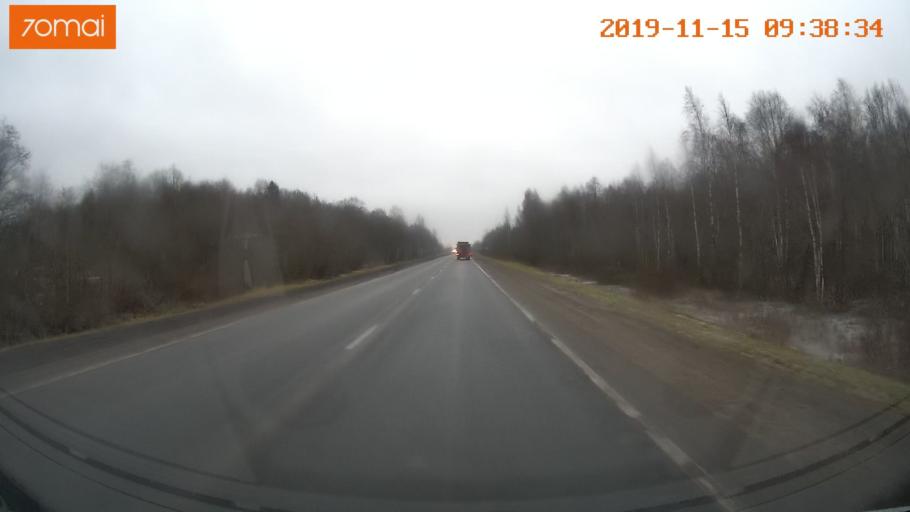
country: RU
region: Vologda
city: Sheksna
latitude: 59.2307
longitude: 38.4582
